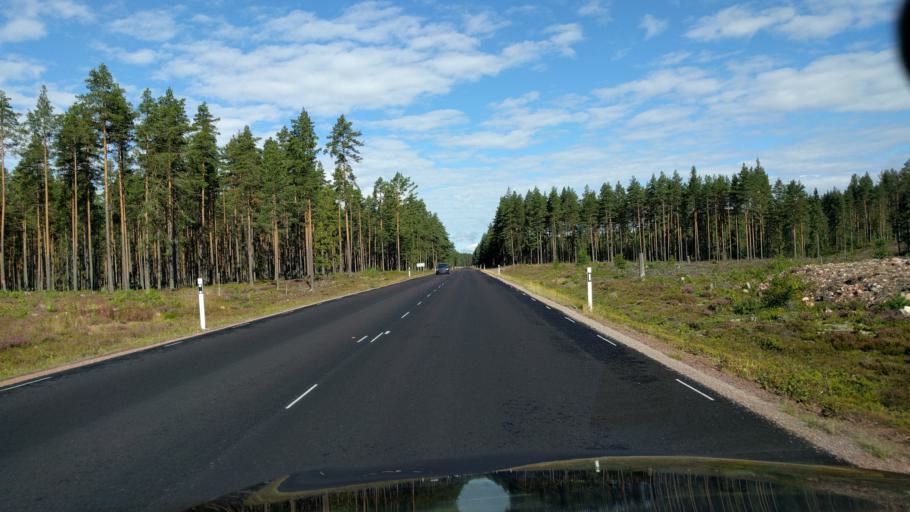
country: SE
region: Dalarna
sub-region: Alvdalens Kommun
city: AElvdalen
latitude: 61.1561
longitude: 14.1293
